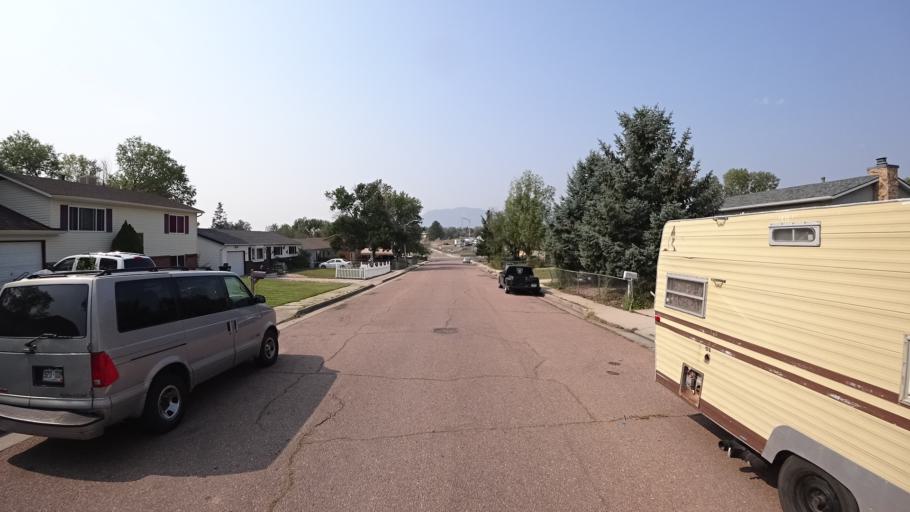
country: US
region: Colorado
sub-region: El Paso County
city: Stratmoor
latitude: 38.8089
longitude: -104.7631
